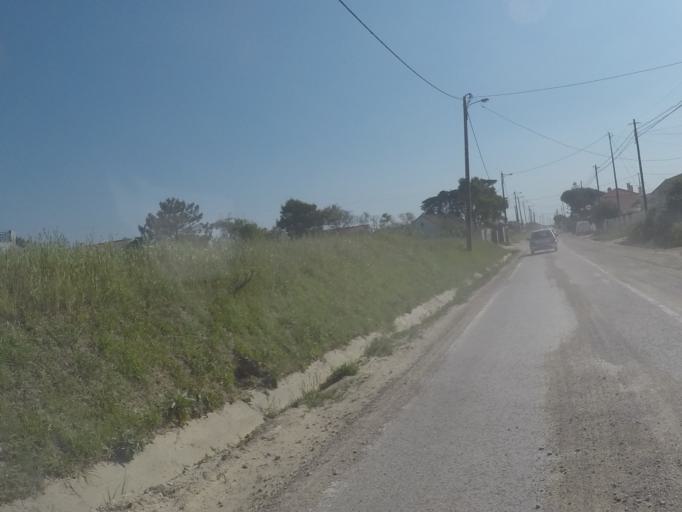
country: PT
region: Setubal
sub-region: Sesimbra
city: Sesimbra
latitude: 38.4296
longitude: -9.1869
